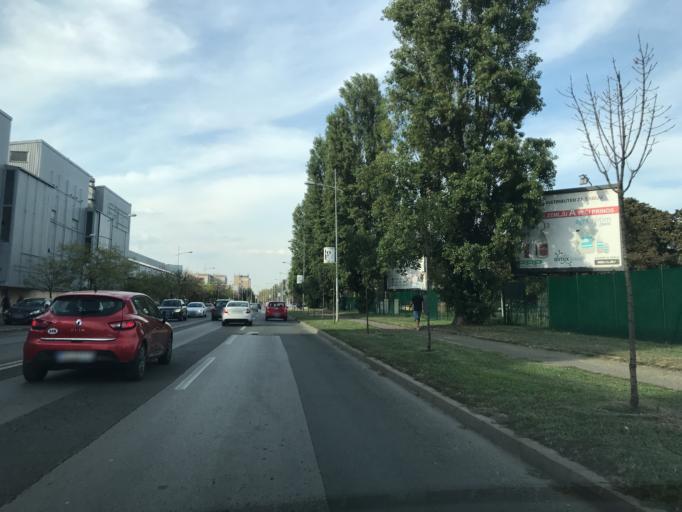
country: RS
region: Autonomna Pokrajina Vojvodina
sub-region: Juznobacki Okrug
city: Novi Sad
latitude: 45.2555
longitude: 19.8244
